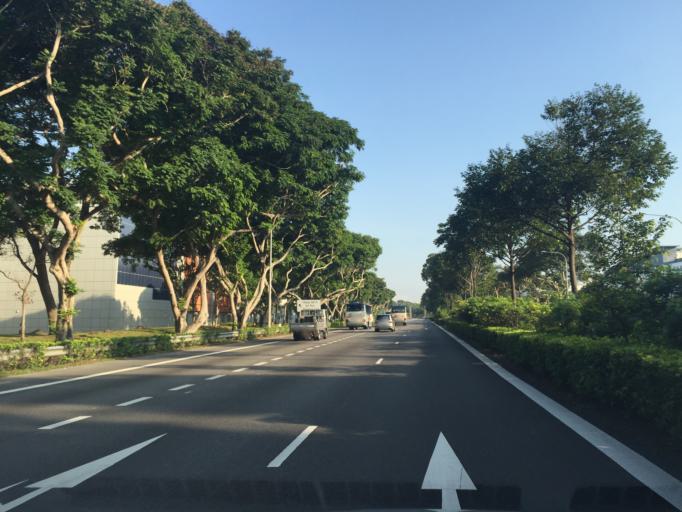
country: SG
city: Singapore
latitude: 1.3438
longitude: 103.9690
